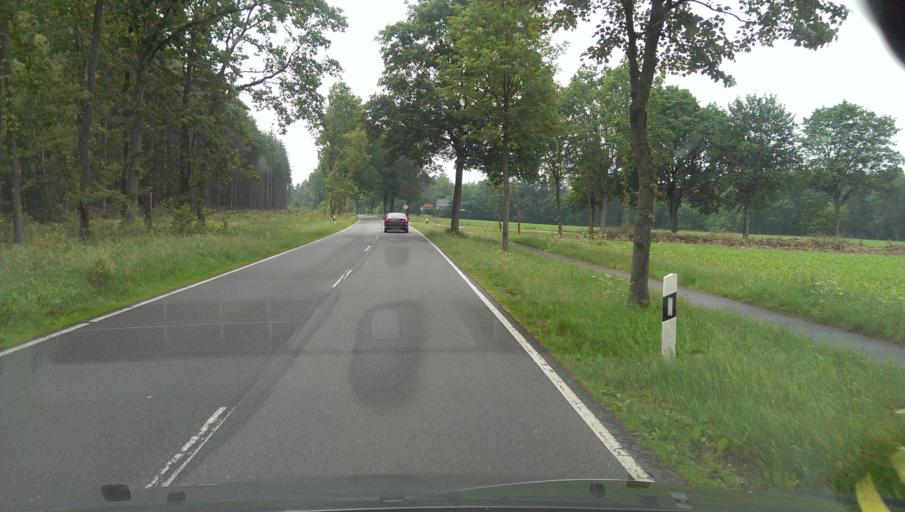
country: DE
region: Lower Saxony
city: Fassberg
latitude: 52.8877
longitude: 10.1759
